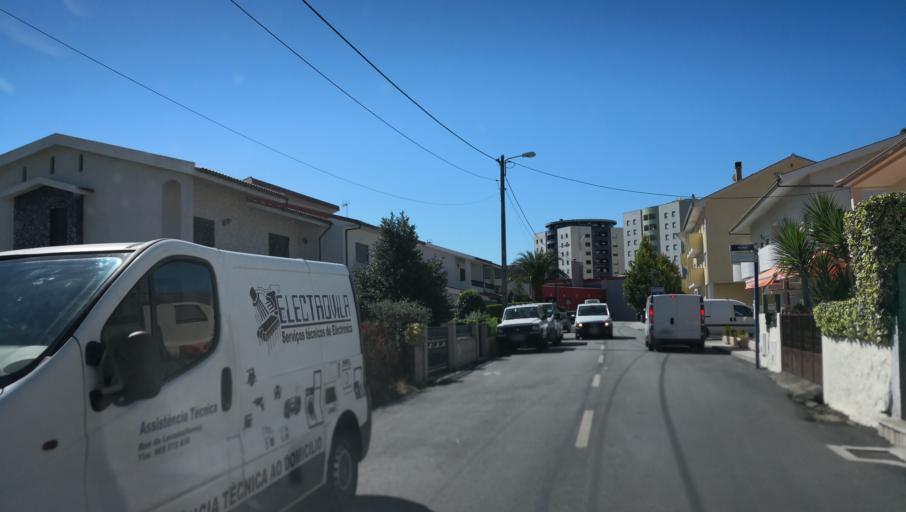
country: PT
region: Vila Real
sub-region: Vila Real
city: Vila Real
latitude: 41.3158
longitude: -7.7295
